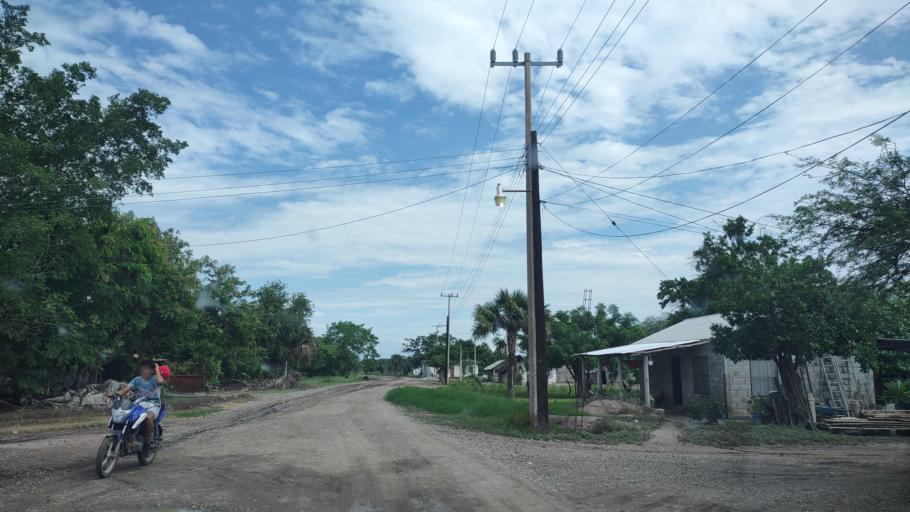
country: MX
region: Veracruz
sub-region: Panuco
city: Oviedo
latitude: 22.0015
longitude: -98.4553
